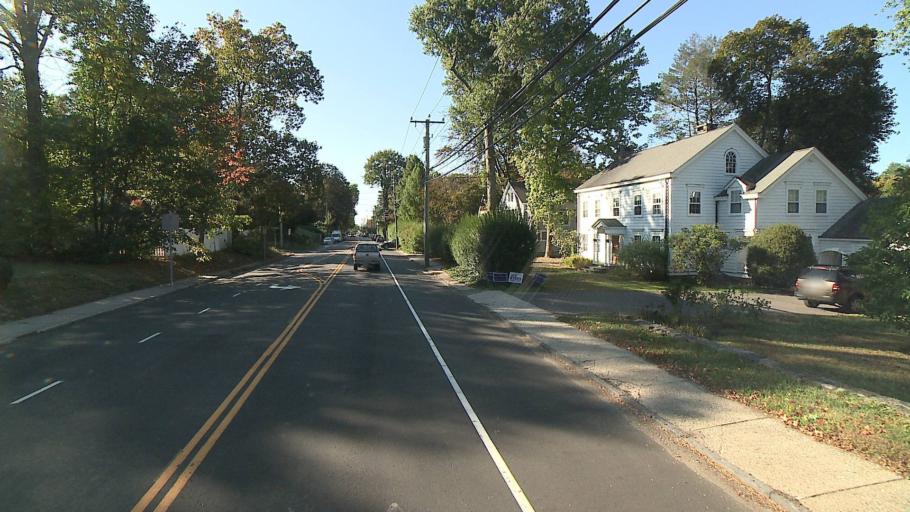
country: US
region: Connecticut
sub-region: Fairfield County
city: Norwalk
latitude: 41.1255
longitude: -73.4055
